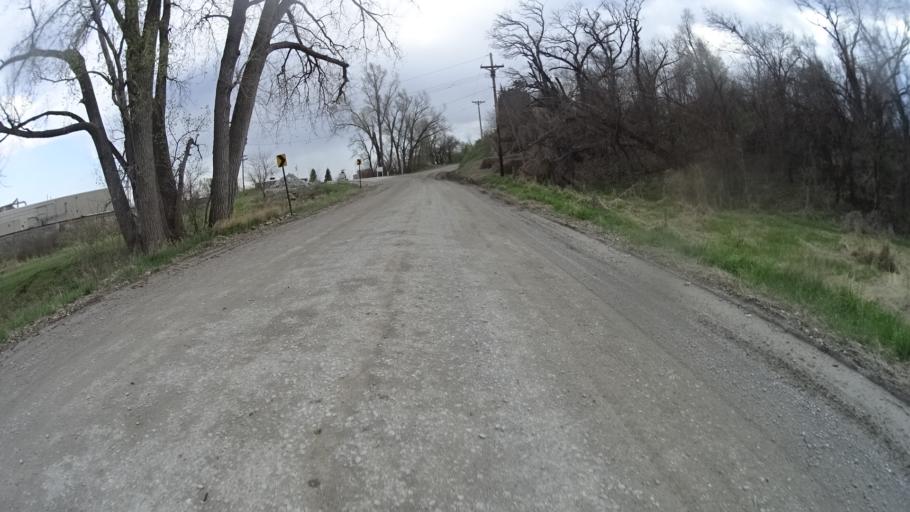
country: US
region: Nebraska
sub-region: Sarpy County
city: Offutt Air Force Base
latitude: 41.0990
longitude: -95.9139
